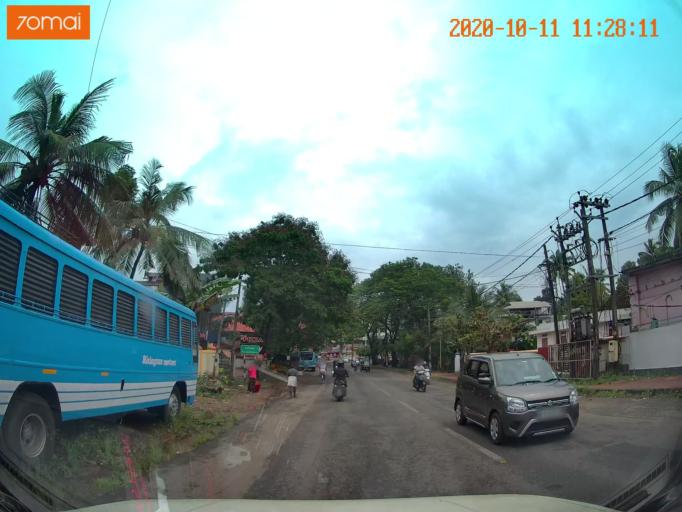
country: IN
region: Kerala
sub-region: Kottayam
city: Changanacheri
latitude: 9.4572
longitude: 76.5528
